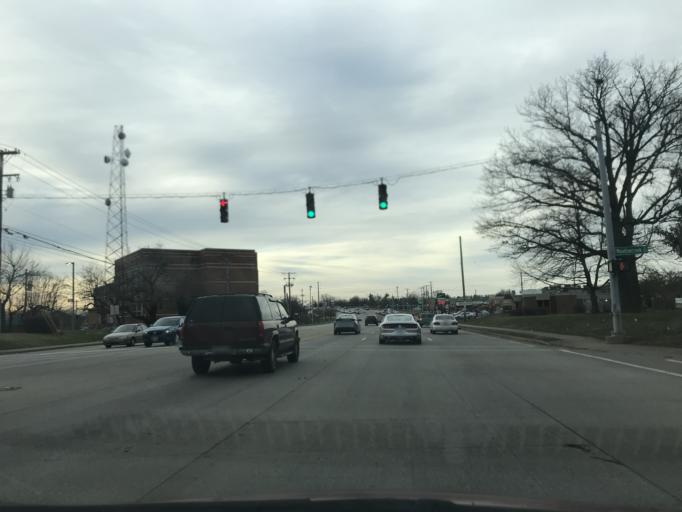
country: US
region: Kentucky
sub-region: Jefferson County
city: West Buechel
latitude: 38.1989
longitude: -85.6833
